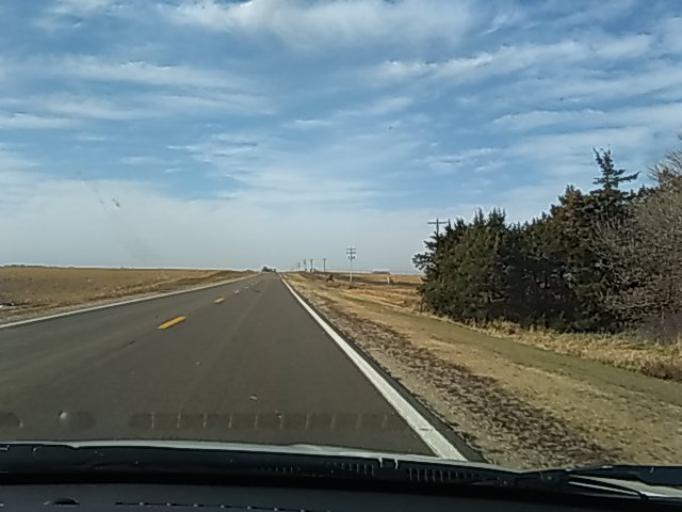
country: US
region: Nebraska
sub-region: Clay County
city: Clay Center
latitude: 40.4232
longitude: -97.9659
